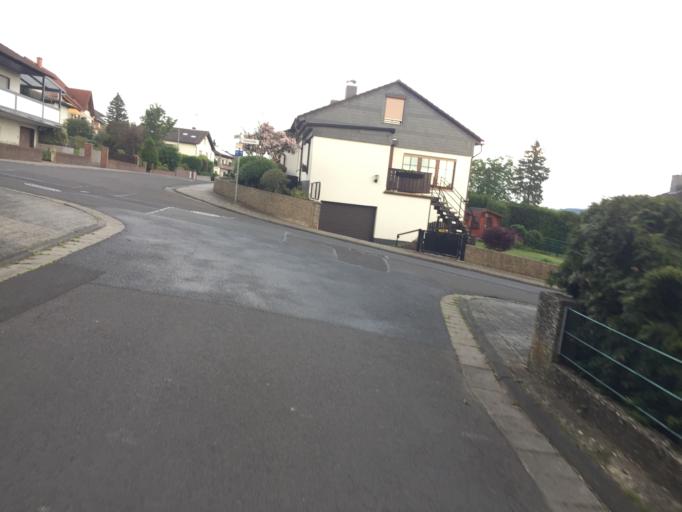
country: DE
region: Hesse
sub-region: Regierungsbezirk Darmstadt
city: Rockenberg
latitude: 50.4436
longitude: 8.7086
